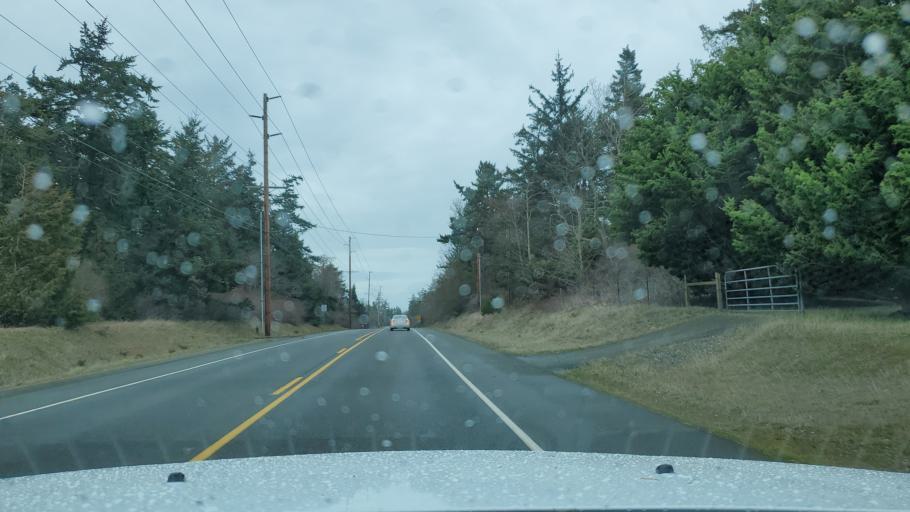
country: US
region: Washington
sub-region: Island County
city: Coupeville
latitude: 48.2515
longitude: -122.7516
